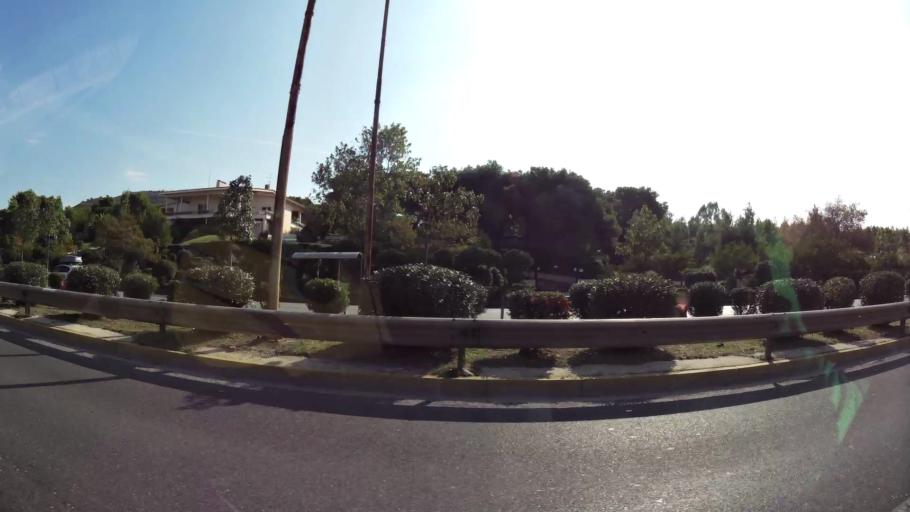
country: GR
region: Attica
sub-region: Nomarchia Athinas
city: Nea Ionia
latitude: 38.0241
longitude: 23.7599
